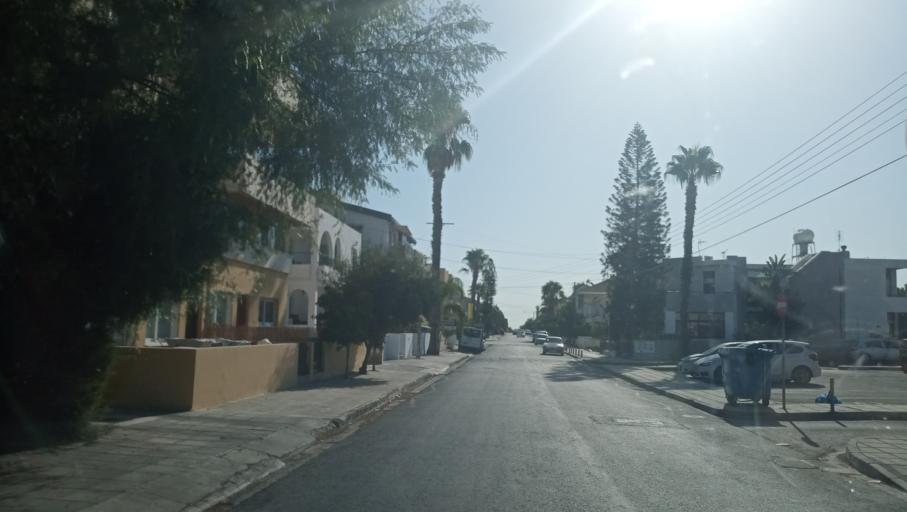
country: CY
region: Lefkosia
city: Nicosia
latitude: 35.1475
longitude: 33.3961
